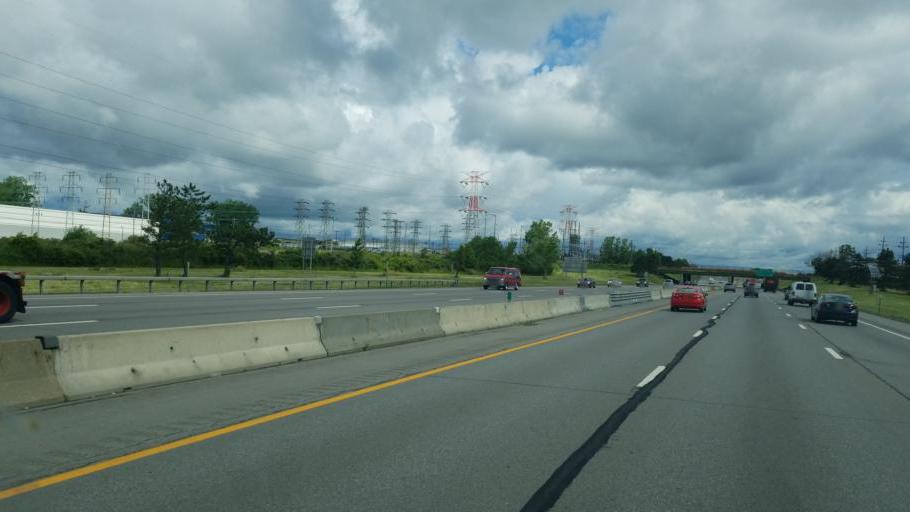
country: US
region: New York
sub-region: Erie County
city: Cheektowaga
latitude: 42.8996
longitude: -78.7670
